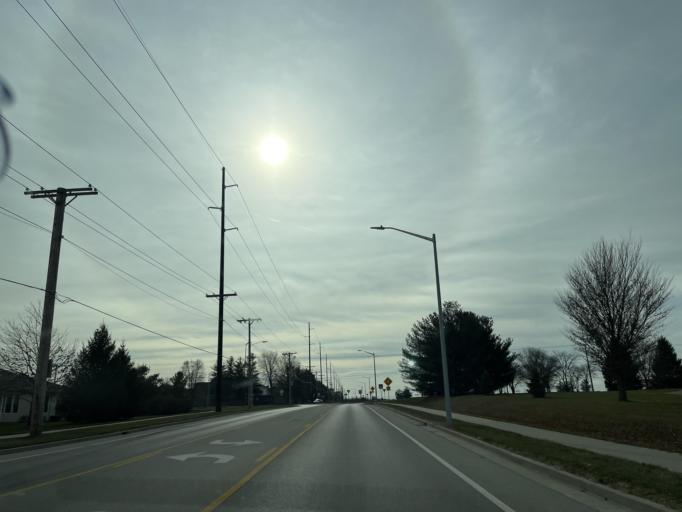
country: US
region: Illinois
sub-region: Sangamon County
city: Jerome
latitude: 39.7722
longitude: -89.7347
